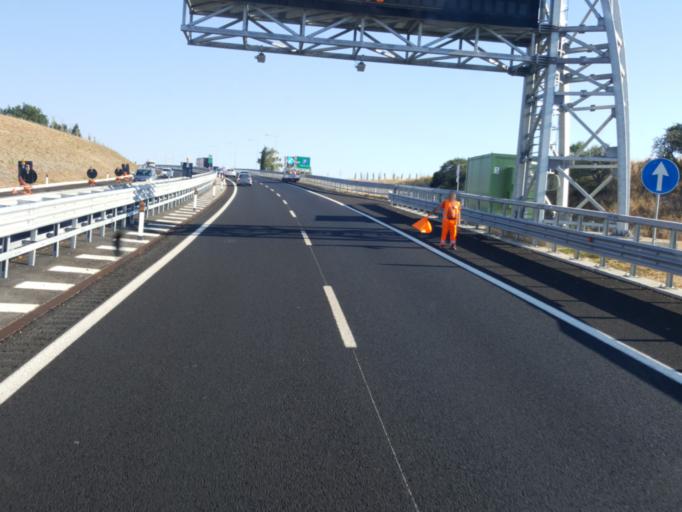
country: IT
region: Latium
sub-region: Citta metropolitana di Roma Capitale
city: Aurelia
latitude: 42.1883
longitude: 11.7866
